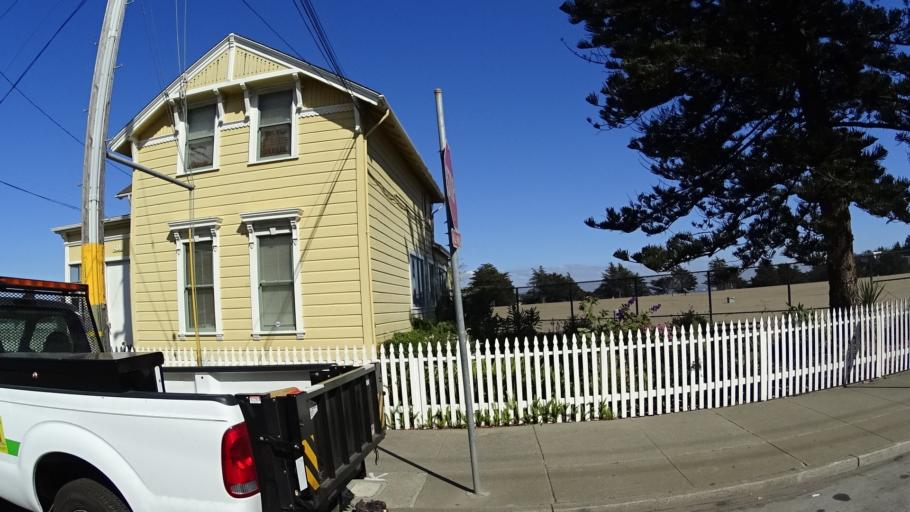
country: US
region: California
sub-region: San Mateo County
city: Brisbane
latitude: 37.7250
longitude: -122.4134
